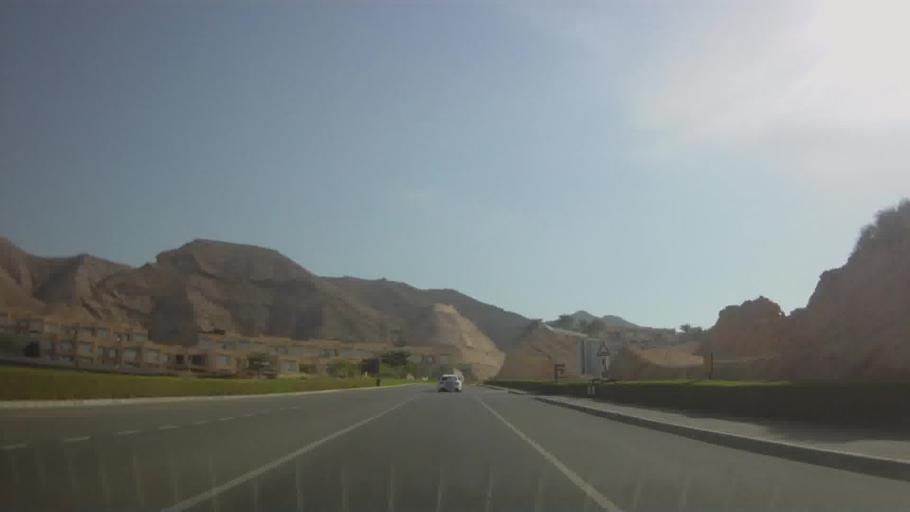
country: OM
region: Muhafazat Masqat
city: Muscat
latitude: 23.5493
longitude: 58.6577
